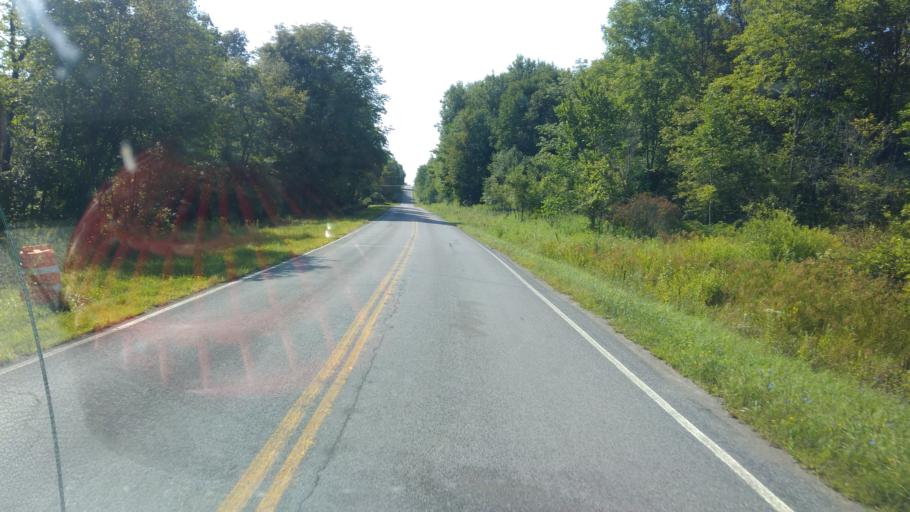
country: US
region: New York
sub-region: Allegany County
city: Friendship
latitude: 42.1675
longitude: -78.1503
